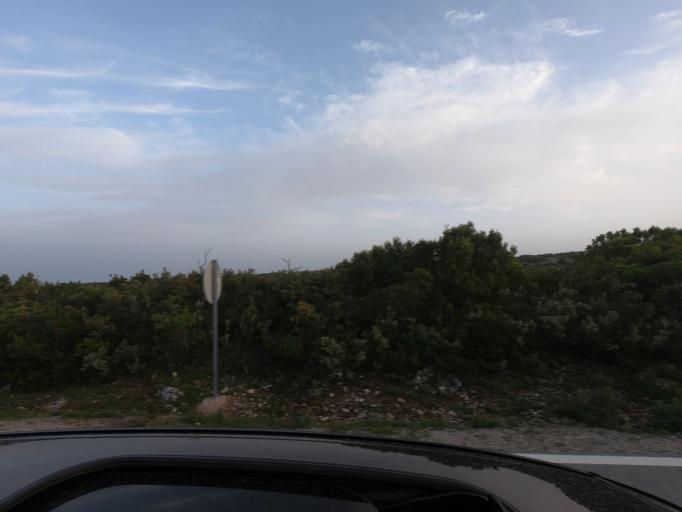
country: PT
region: Setubal
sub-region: Palmela
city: Quinta do Anjo
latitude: 38.4940
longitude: -8.9679
